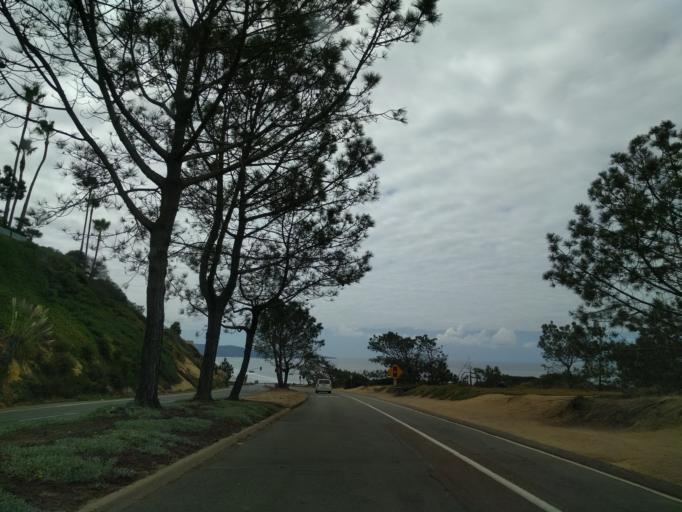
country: US
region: California
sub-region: San Diego County
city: Del Mar
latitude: 32.9422
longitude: -117.2610
